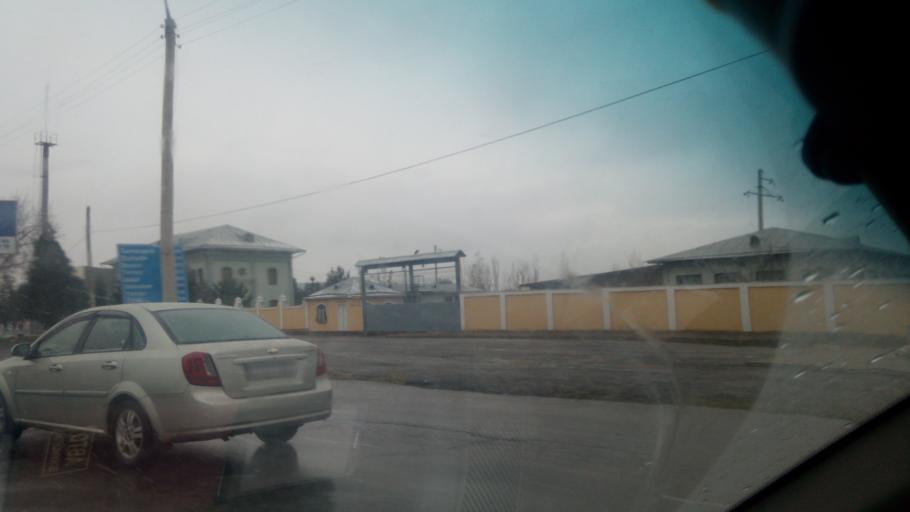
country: UZ
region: Toshkent
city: Urtaowul
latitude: 41.2357
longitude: 69.1647
